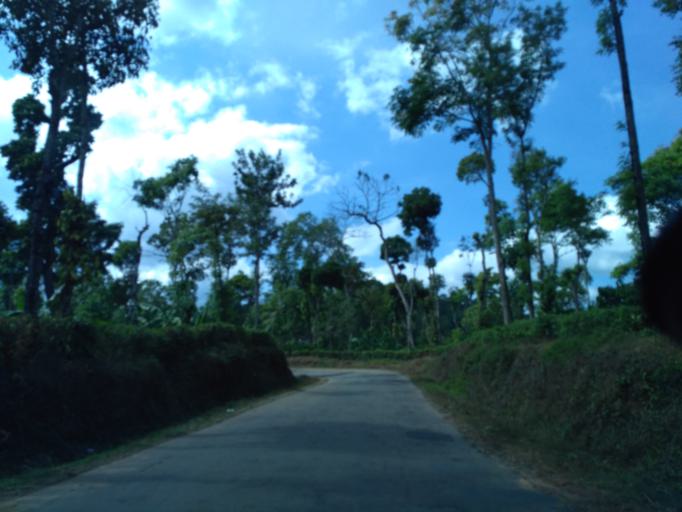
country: IN
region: Karnataka
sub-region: Kodagu
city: Madikeri
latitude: 12.3545
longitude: 75.6793
